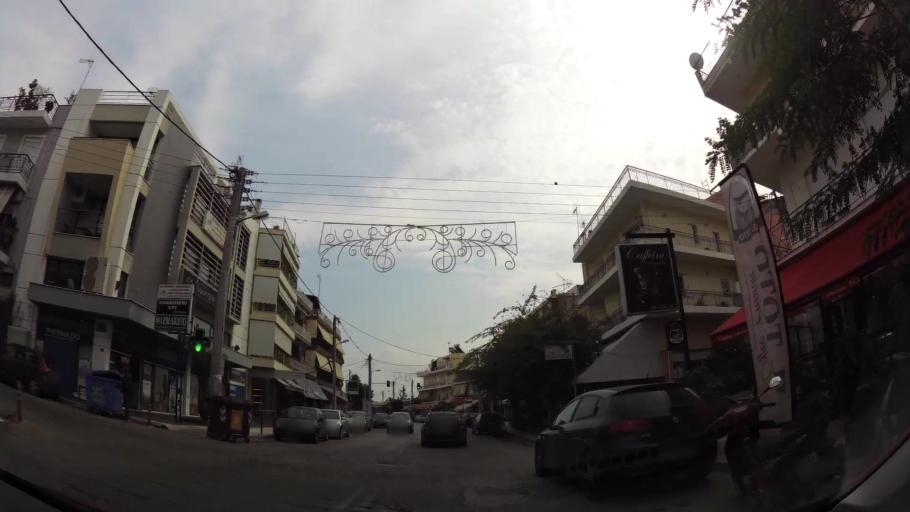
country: GR
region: Attica
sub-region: Nomarchia Athinas
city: Peristeri
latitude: 38.0069
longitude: 23.6833
